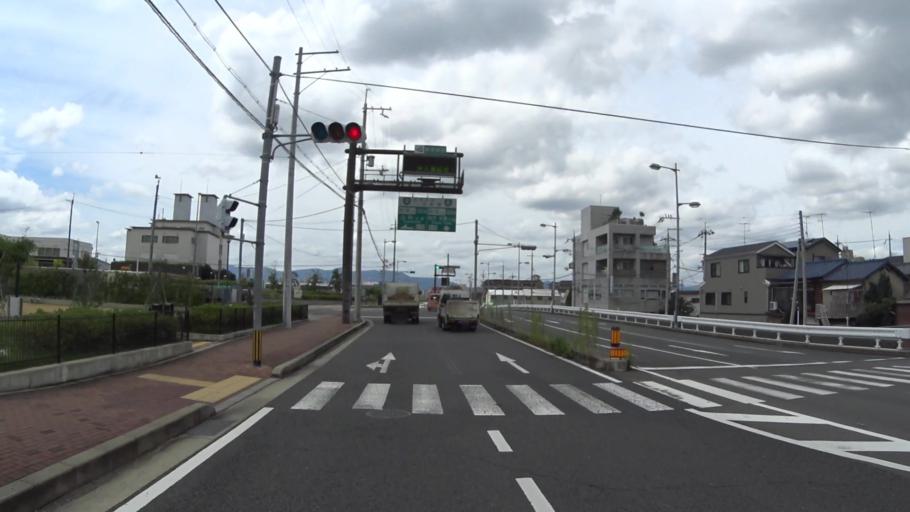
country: JP
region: Kyoto
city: Kyoto
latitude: 34.9730
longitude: 135.7682
